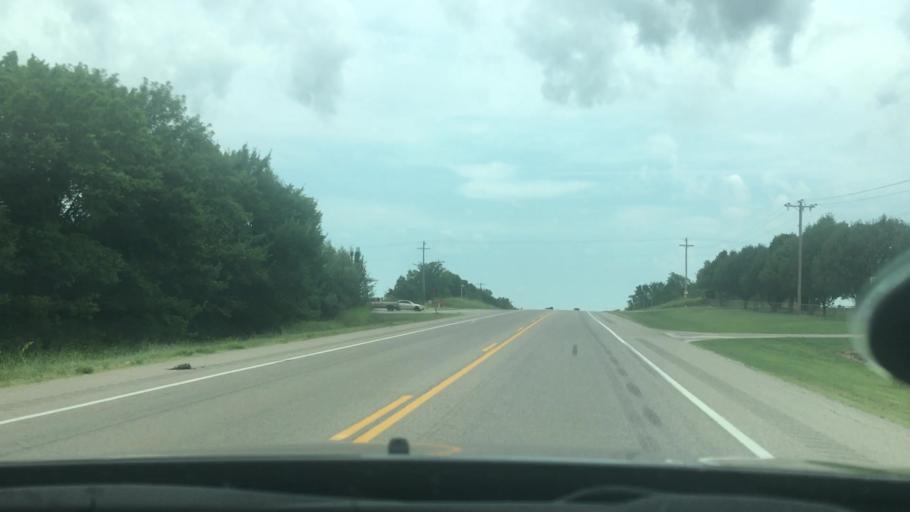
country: US
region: Oklahoma
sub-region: Seminole County
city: Konawa
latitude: 34.9838
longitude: -96.6793
